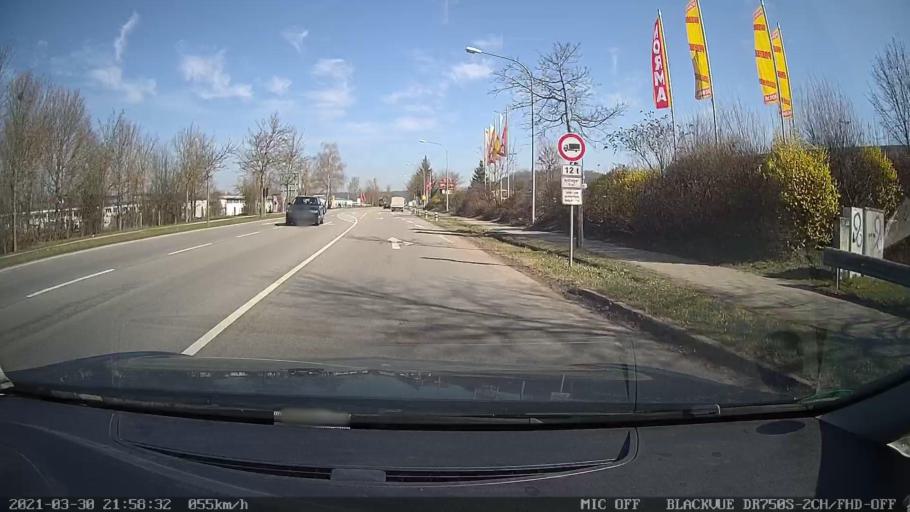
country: DE
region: Bavaria
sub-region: Upper Palatinate
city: Regenstauf
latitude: 49.1139
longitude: 12.1251
